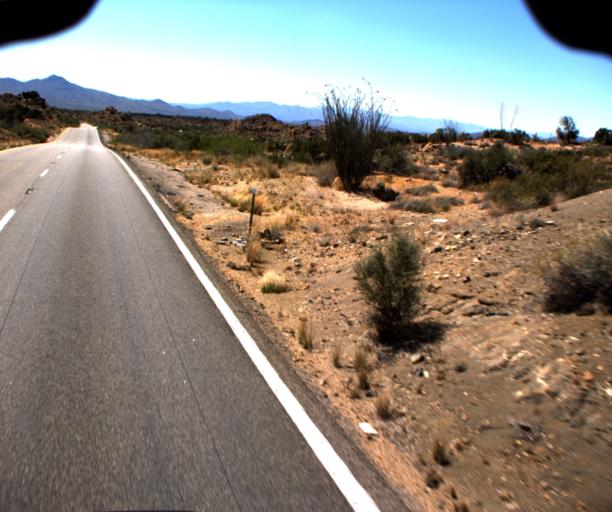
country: US
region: Arizona
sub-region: Yavapai County
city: Bagdad
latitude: 34.4839
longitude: -113.3557
